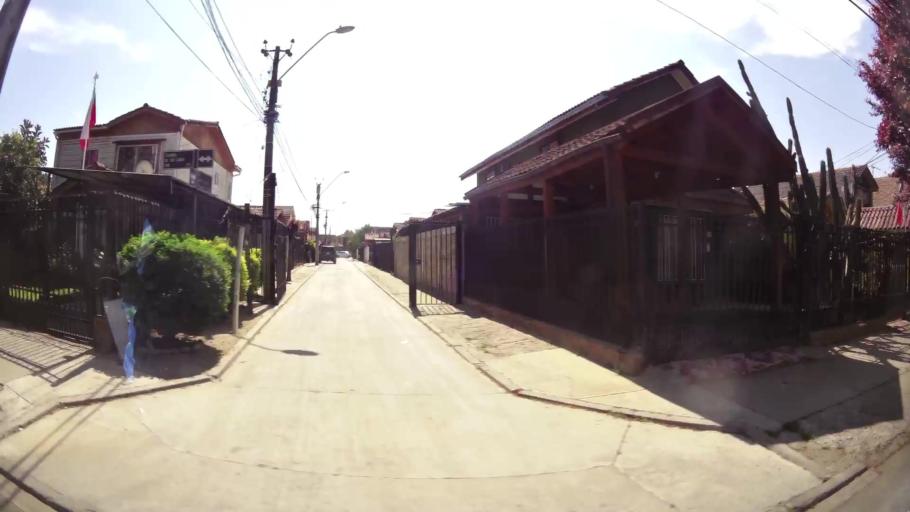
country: CL
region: Santiago Metropolitan
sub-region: Provincia de Santiago
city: Lo Prado
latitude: -33.4687
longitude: -70.7356
